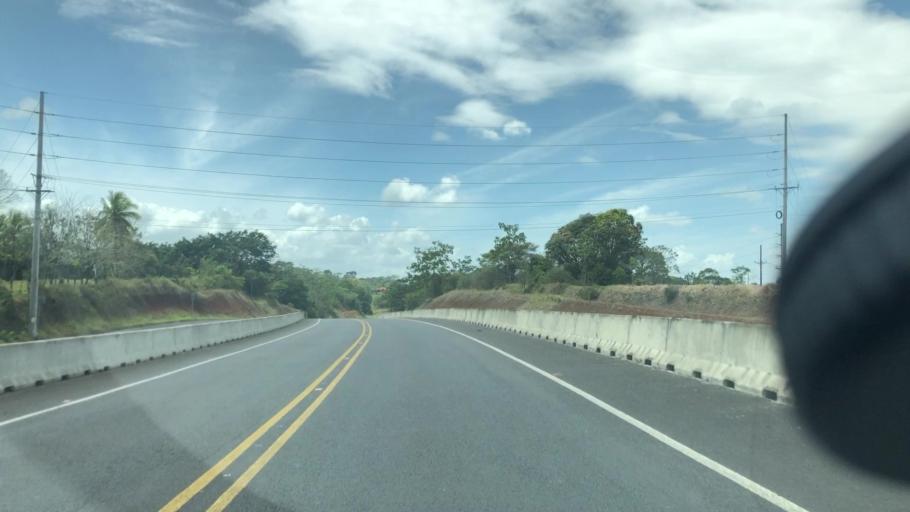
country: CR
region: Heredia
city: La Virgen
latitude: 10.4403
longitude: -84.1602
